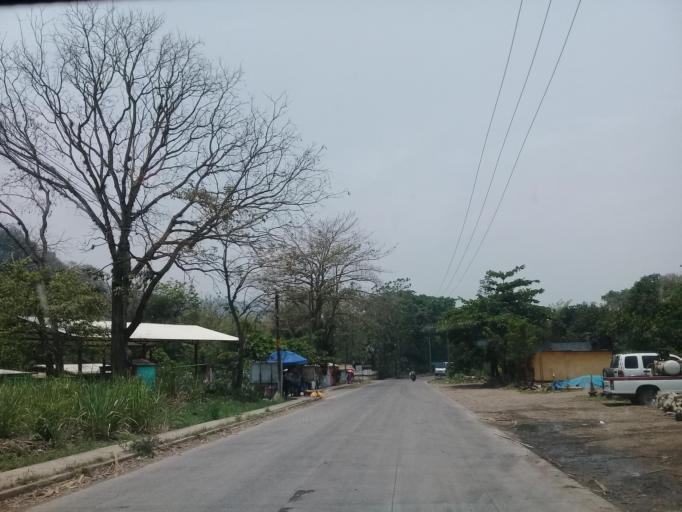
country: MX
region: Veracruz
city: Cosolapa
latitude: 18.5922
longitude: -96.6946
